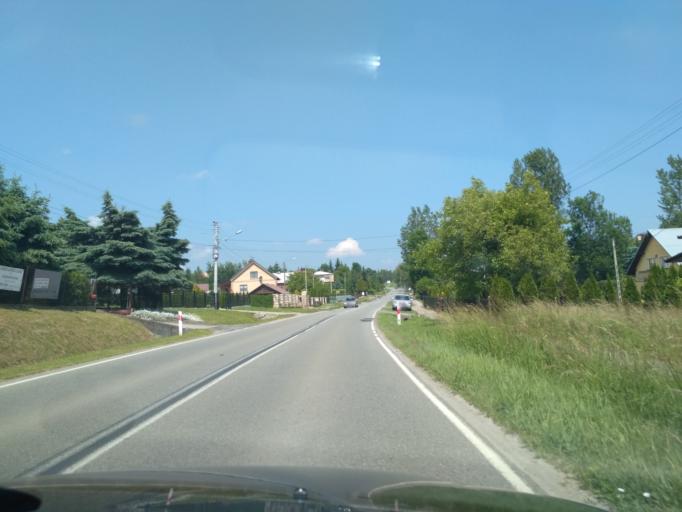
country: PL
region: Subcarpathian Voivodeship
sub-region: Powiat lancucki
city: Lancut
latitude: 50.0453
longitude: 22.2270
